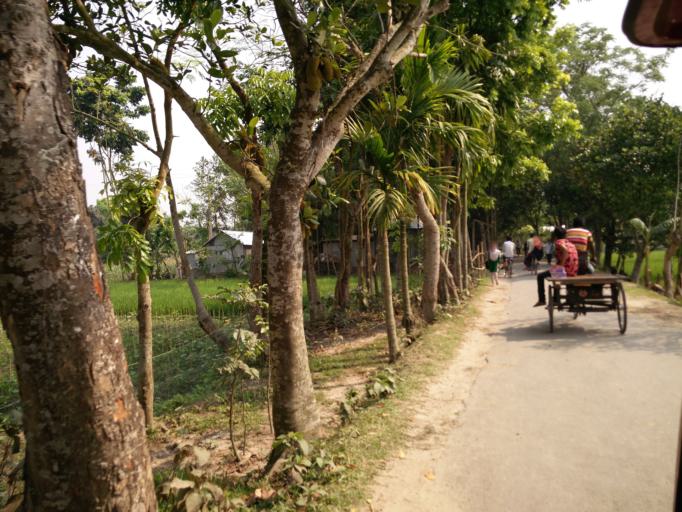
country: BD
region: Dhaka
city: Muktagacha
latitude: 24.9179
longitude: 90.2341
